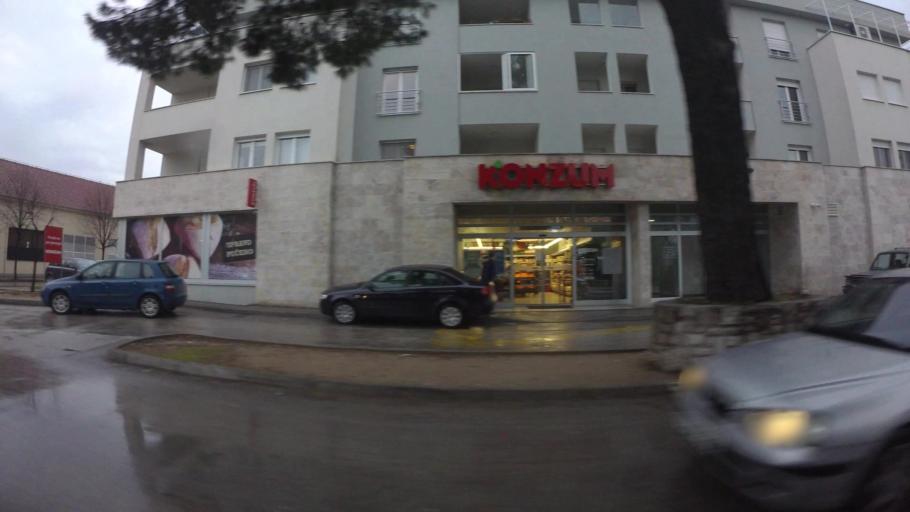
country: BA
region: Federation of Bosnia and Herzegovina
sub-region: Hercegovacko-Bosanski Kanton
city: Mostar
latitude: 43.3552
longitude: 17.7996
